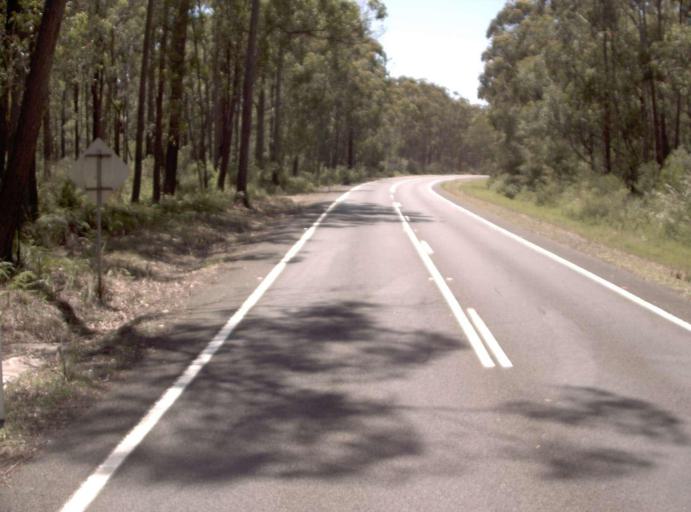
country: AU
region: Victoria
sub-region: East Gippsland
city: Lakes Entrance
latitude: -37.7520
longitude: 148.0680
